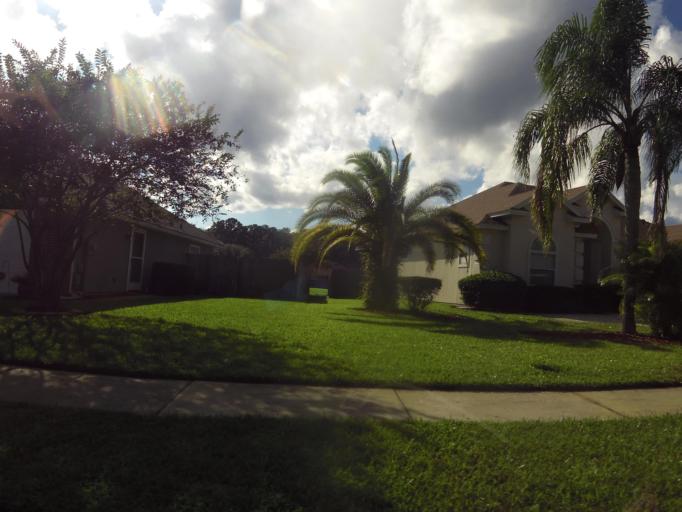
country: US
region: Florida
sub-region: Duval County
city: Jacksonville Beach
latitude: 30.2783
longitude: -81.4974
